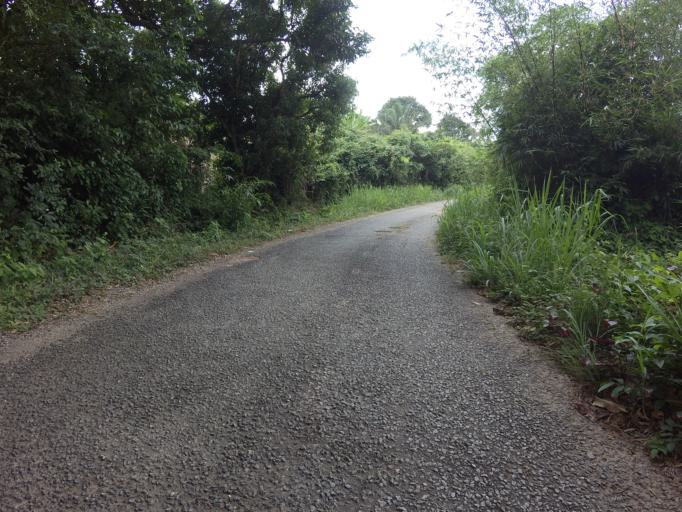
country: GH
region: Volta
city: Kpandu
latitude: 6.8851
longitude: 0.4442
